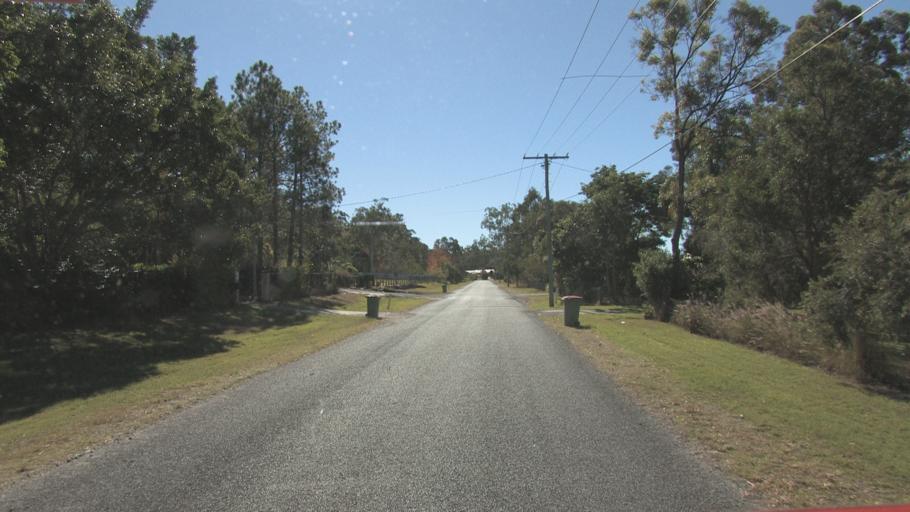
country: AU
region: Queensland
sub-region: Logan
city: Park Ridge South
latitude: -27.7121
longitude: 153.0412
